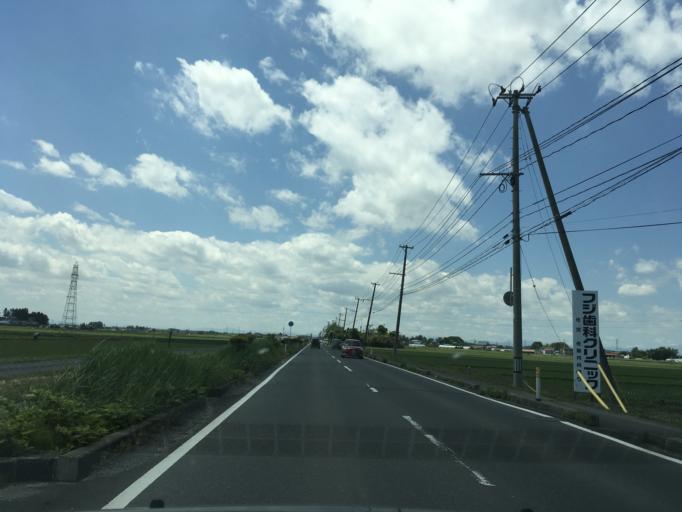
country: JP
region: Miyagi
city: Wakuya
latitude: 38.6782
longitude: 141.2283
